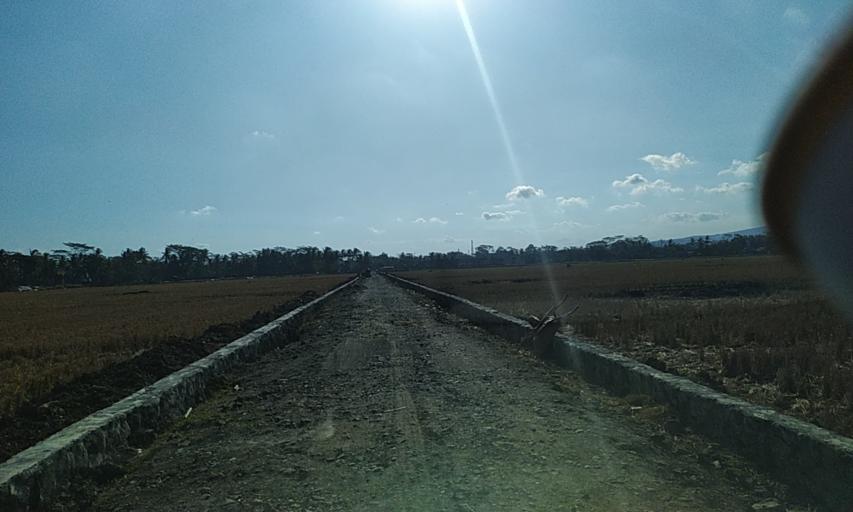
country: ID
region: Central Java
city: Krikil
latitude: -7.6236
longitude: 109.1350
